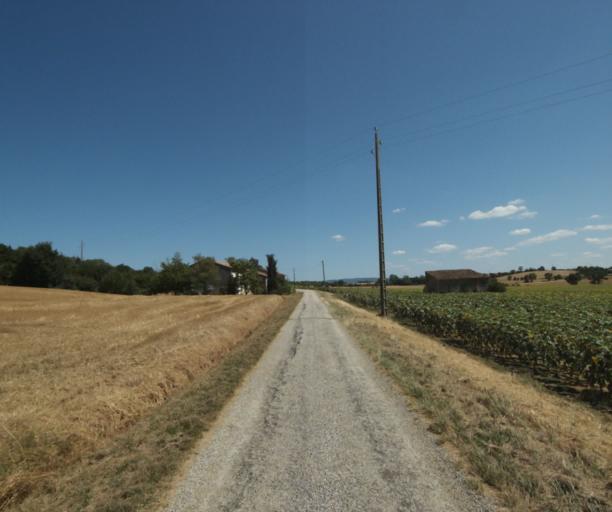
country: FR
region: Midi-Pyrenees
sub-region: Departement de la Haute-Garonne
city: Saint-Felix-Lauragais
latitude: 43.4879
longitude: 1.8908
